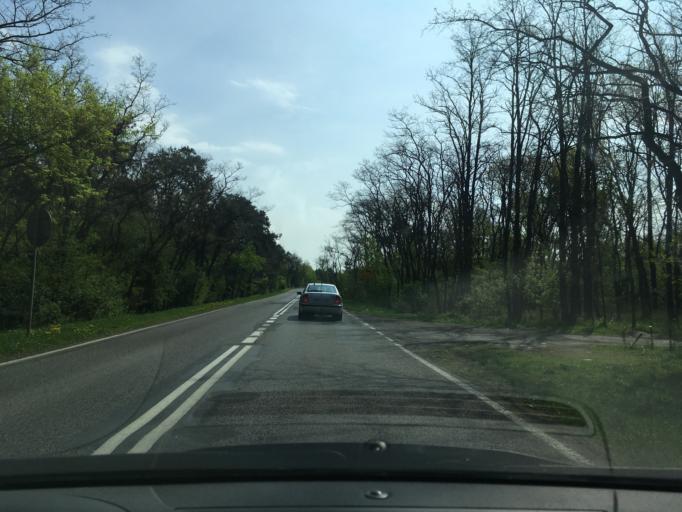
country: PL
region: Lublin Voivodeship
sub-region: Powiat pulawski
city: Pulawy
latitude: 51.4617
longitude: 21.9414
